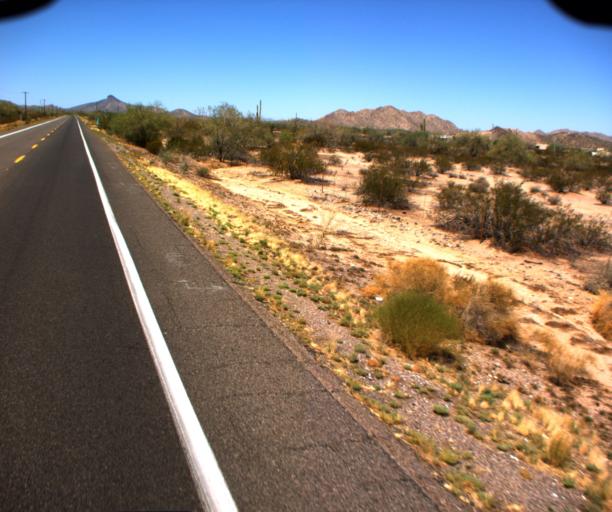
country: US
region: Arizona
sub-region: Pinal County
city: Maricopa
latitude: 32.8516
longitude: -112.0881
